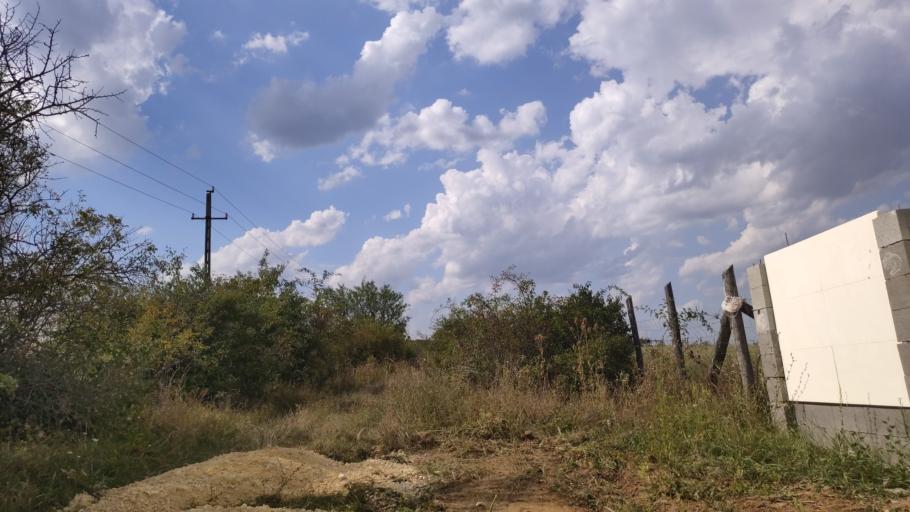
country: HU
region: Pest
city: Toeroekbalint
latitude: 47.4511
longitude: 18.8735
